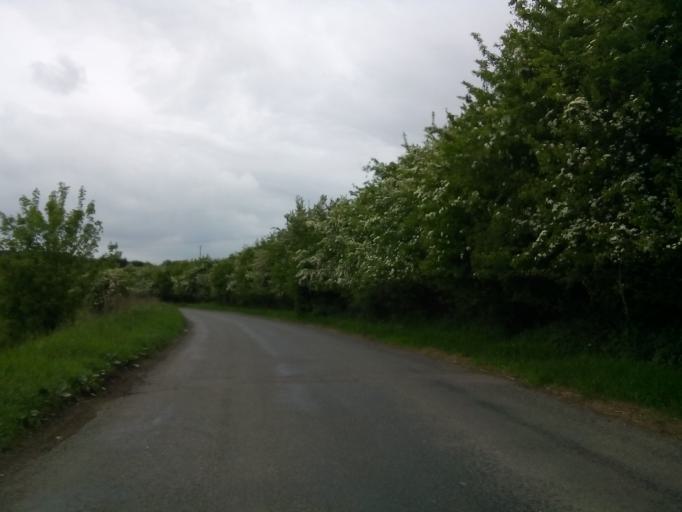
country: GB
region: England
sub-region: Northamptonshire
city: Oundle
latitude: 52.5236
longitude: -0.5463
